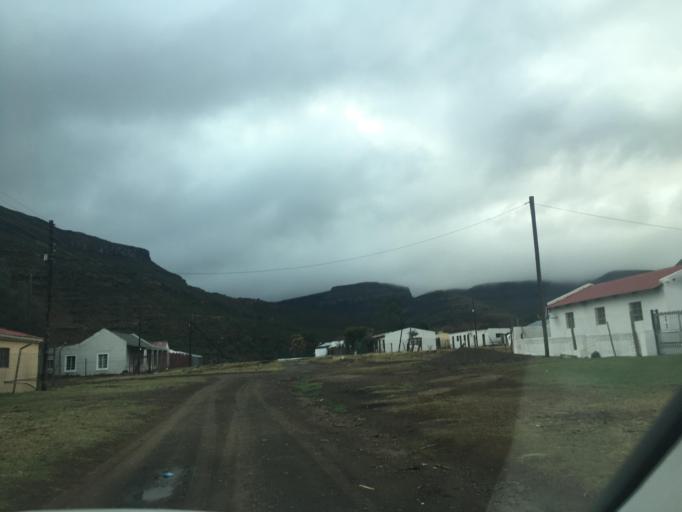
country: ZA
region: Eastern Cape
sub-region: Chris Hani District Municipality
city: Cala
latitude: -31.5217
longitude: 27.7026
